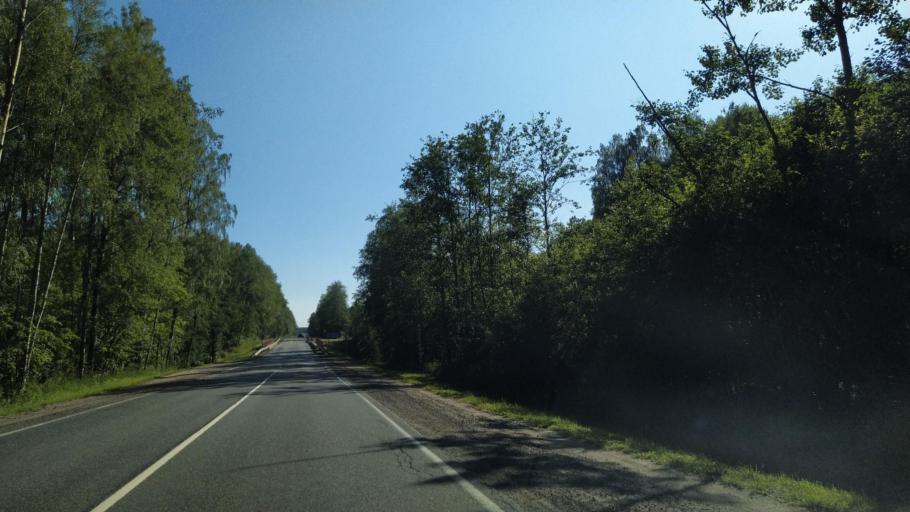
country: RU
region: Leningrad
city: Kirovsk
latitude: 59.9235
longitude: 30.9474
